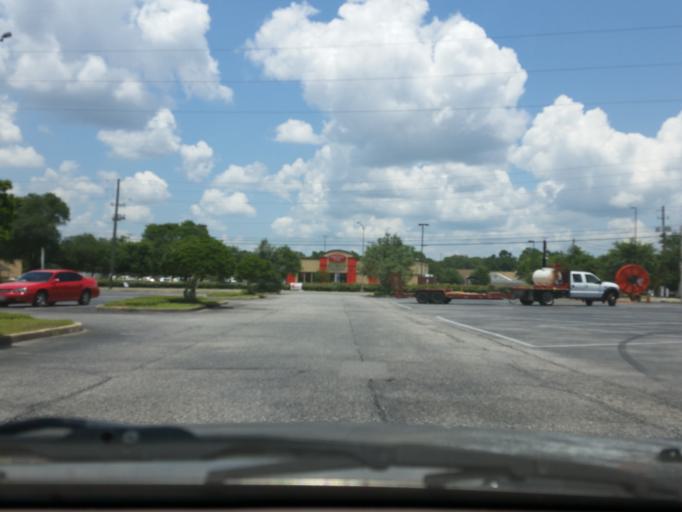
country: US
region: Florida
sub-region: Escambia County
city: Ferry Pass
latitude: 30.4944
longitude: -87.1917
